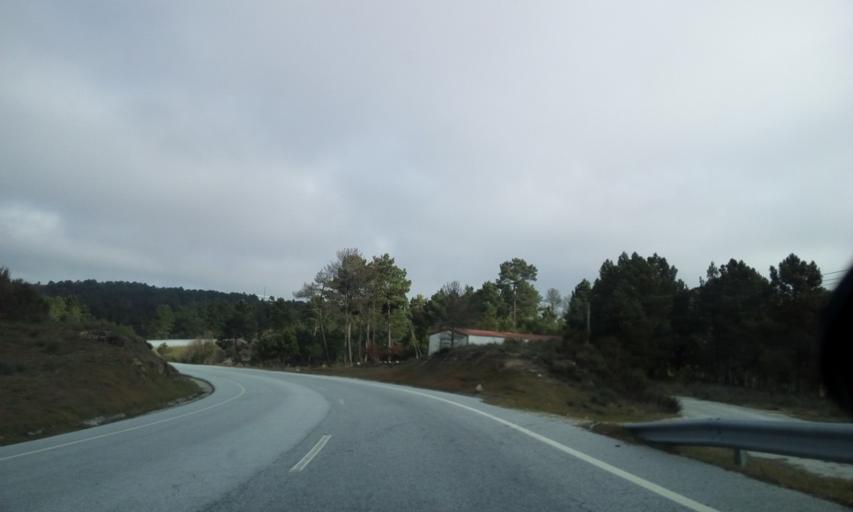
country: PT
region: Guarda
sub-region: Aguiar da Beira
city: Aguiar da Beira
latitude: 40.7774
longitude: -7.5047
